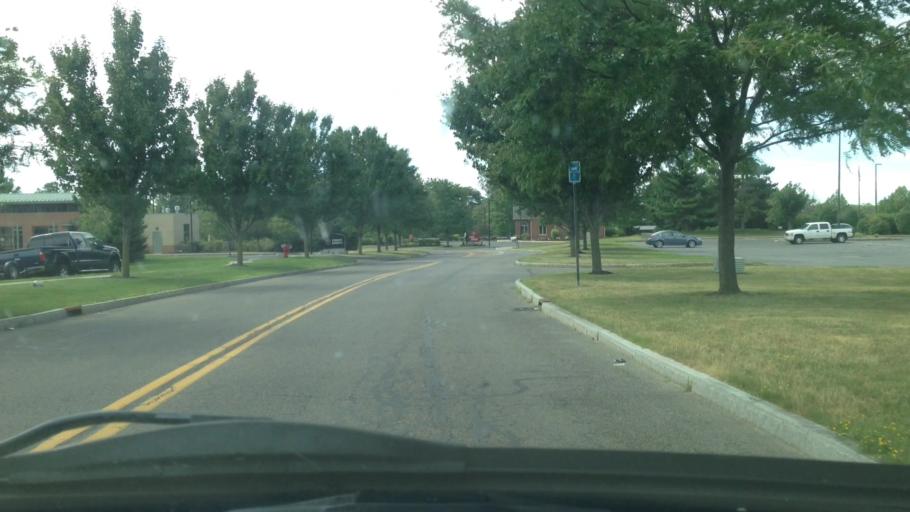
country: US
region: New York
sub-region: Onondaga County
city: East Syracuse
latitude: 43.0892
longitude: -76.0802
